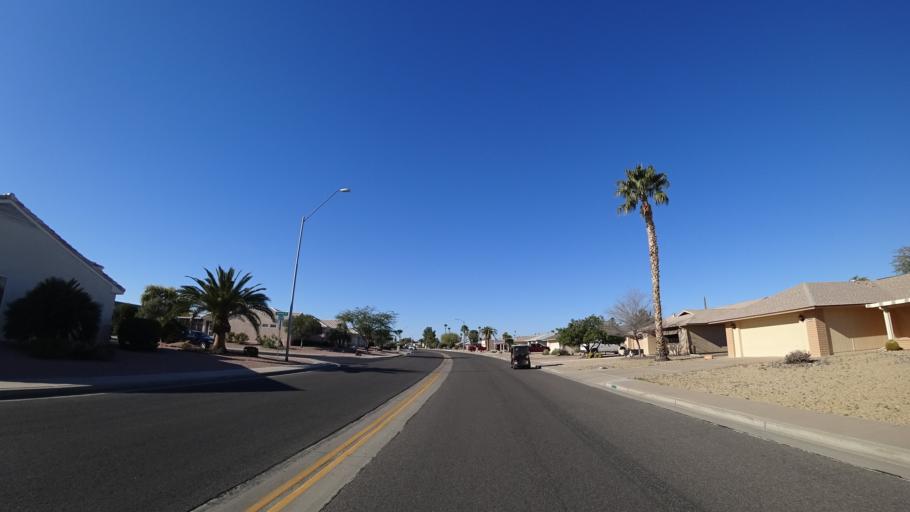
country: US
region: Arizona
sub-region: Maricopa County
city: Sun City West
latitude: 33.6679
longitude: -112.3410
